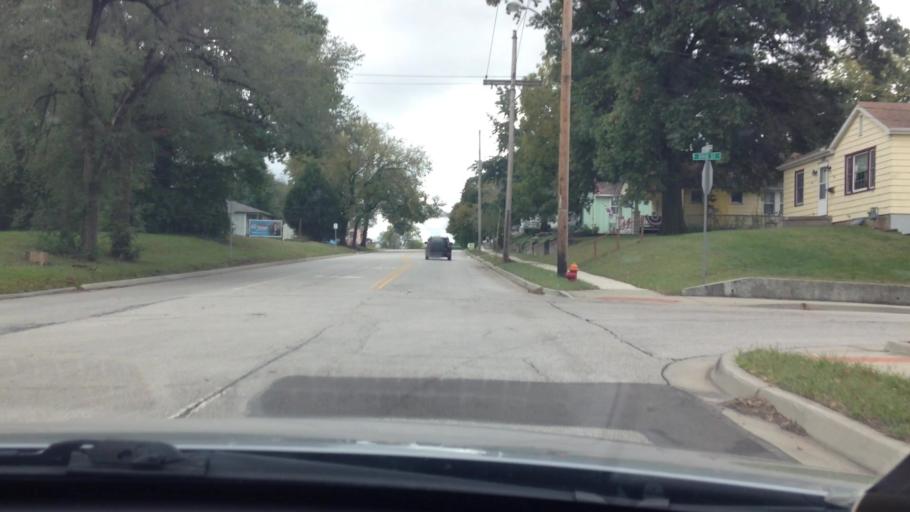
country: US
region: Kansas
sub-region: Leavenworth County
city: Leavenworth
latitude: 39.3032
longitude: -94.9275
